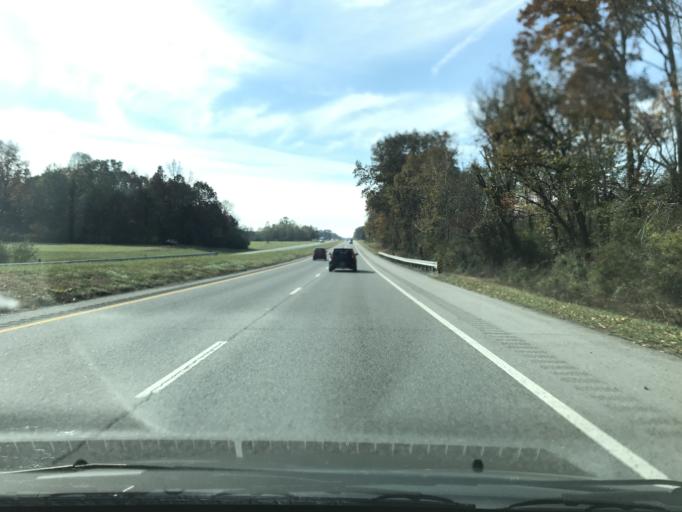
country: US
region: Tennessee
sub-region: Coffee County
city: Manchester
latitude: 35.4355
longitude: -86.1042
